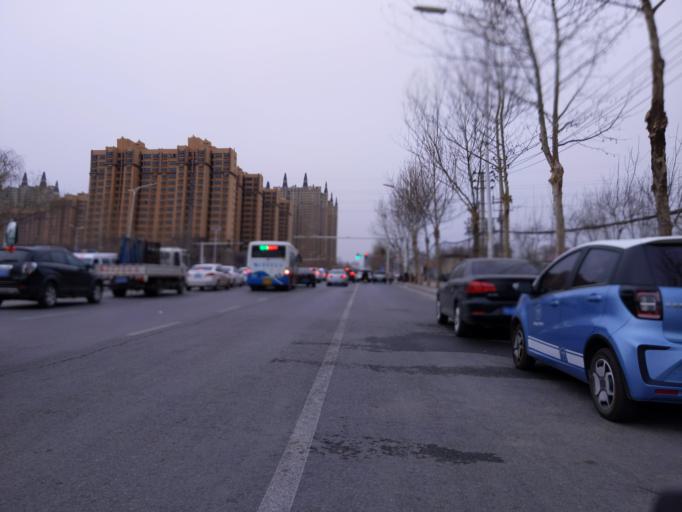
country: CN
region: Henan Sheng
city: Zhongyuanlu
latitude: 35.7455
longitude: 115.0655
